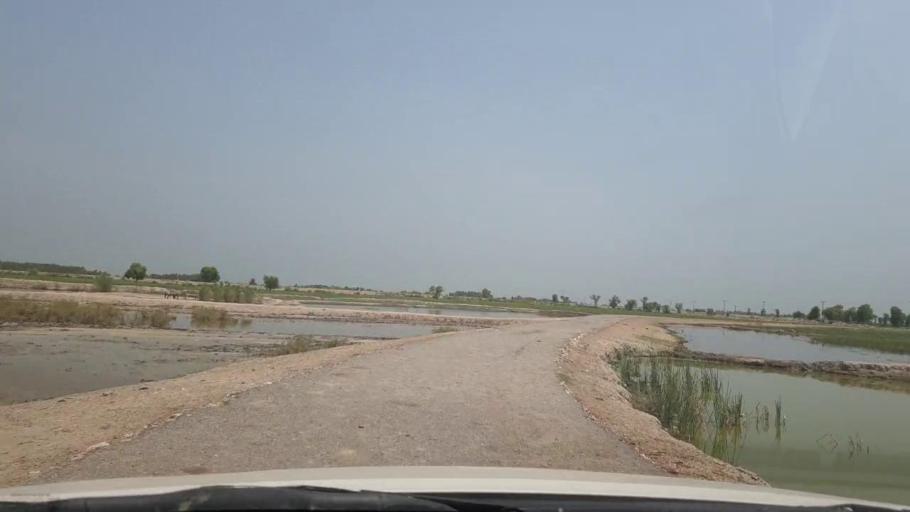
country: PK
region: Sindh
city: Rustam jo Goth
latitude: 28.0184
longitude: 68.7835
